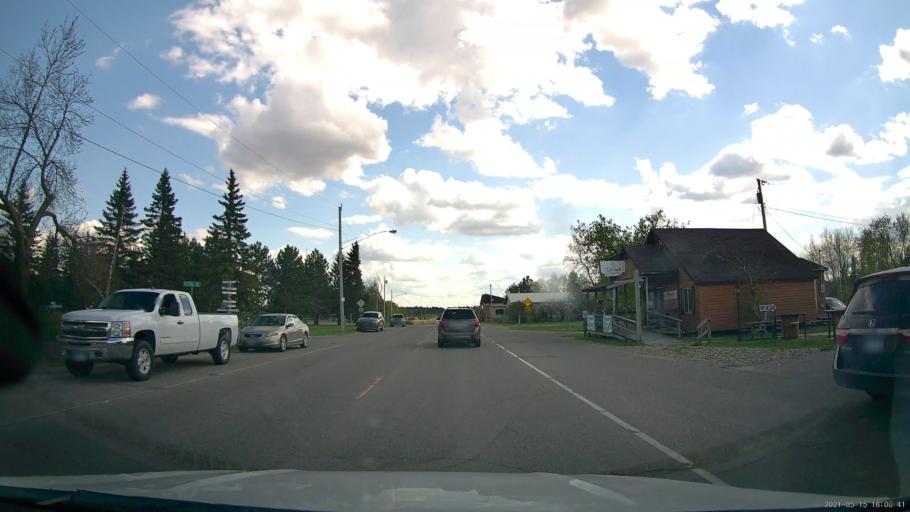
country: US
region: Minnesota
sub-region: Hubbard County
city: Park Rapids
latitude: 46.9567
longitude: -94.9527
